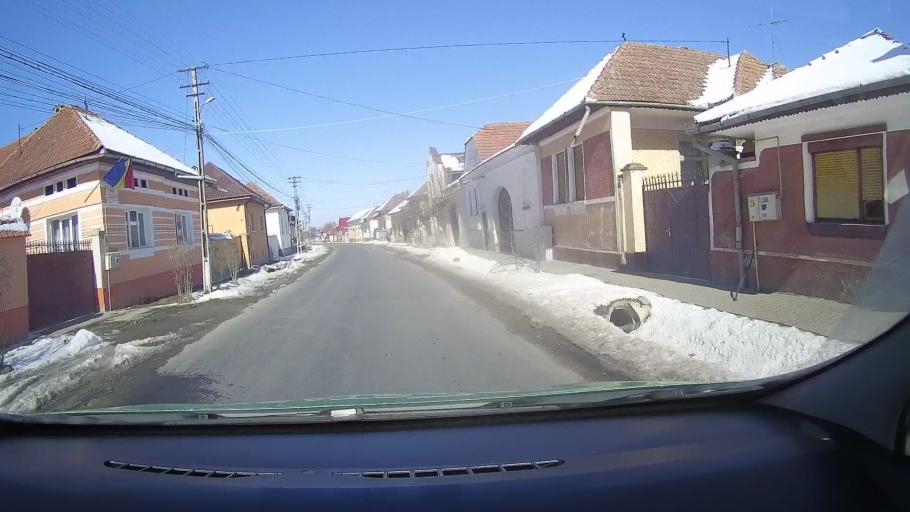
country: RO
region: Brasov
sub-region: Comuna Harseni
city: Harseni
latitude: 45.7902
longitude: 24.9975
